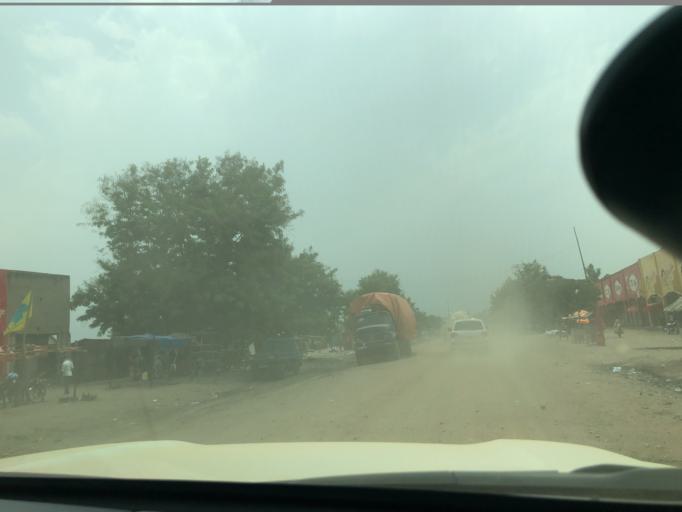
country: UG
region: Western Region
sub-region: Kasese District
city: Margherita
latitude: 0.3300
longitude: 29.6752
